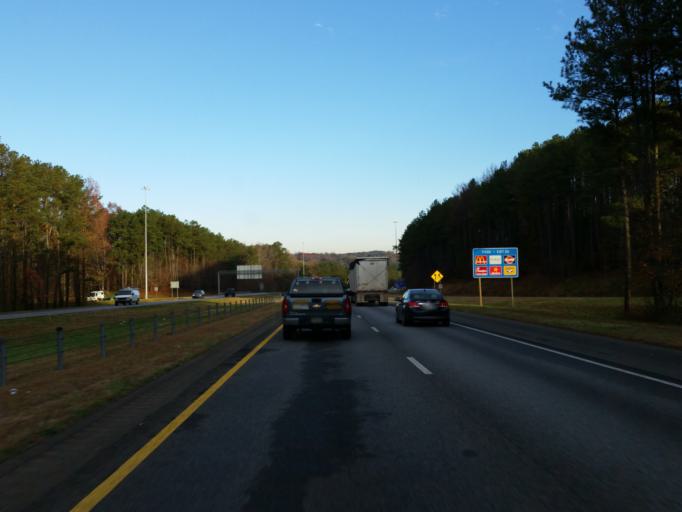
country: US
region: Georgia
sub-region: Cherokee County
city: Canton
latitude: 34.2417
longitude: -84.4663
